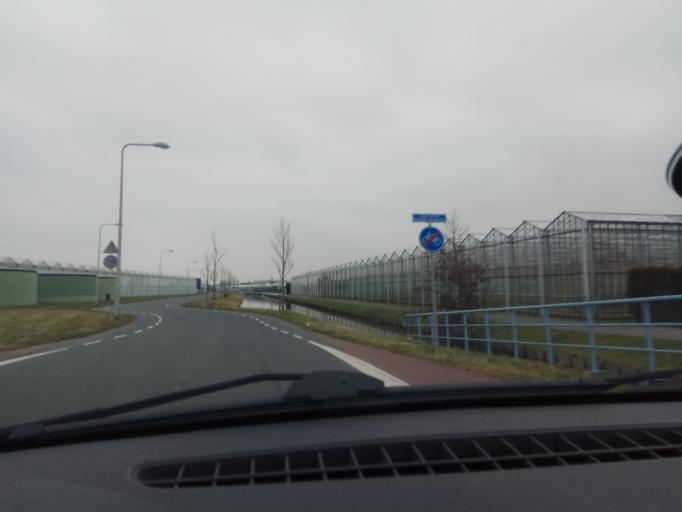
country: NL
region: South Holland
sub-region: Gemeente Westland
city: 's-Gravenzande
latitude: 51.9864
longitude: 4.1839
